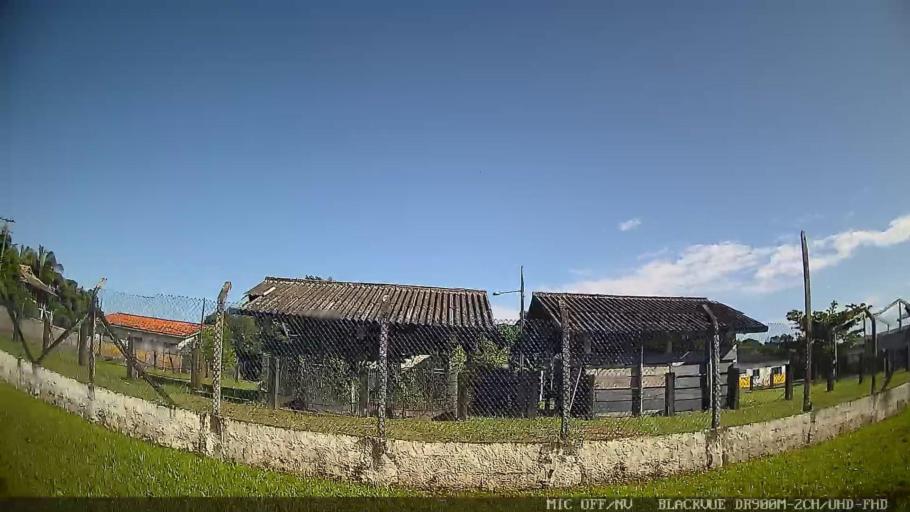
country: BR
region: Sao Paulo
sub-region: Peruibe
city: Peruibe
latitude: -24.2689
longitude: -46.9443
